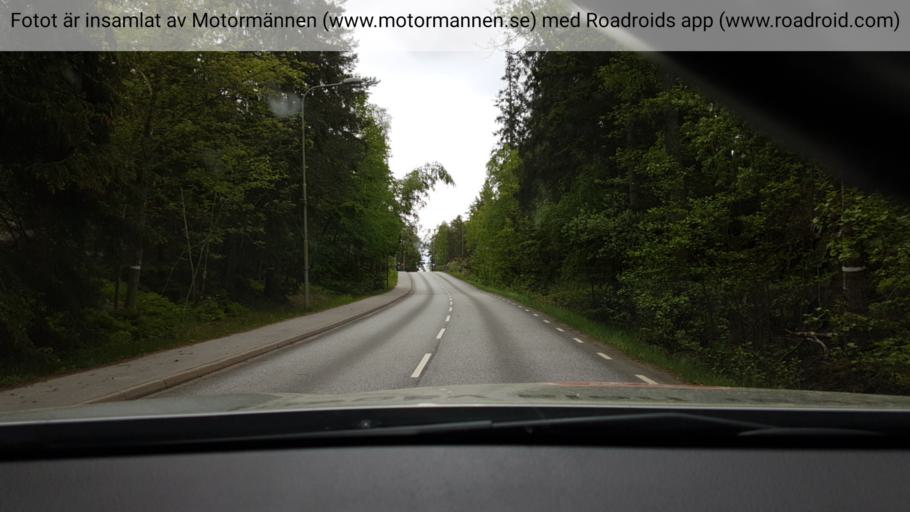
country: SE
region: Stockholm
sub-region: Nacka Kommun
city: Saltsjobaden
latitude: 59.2618
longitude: 18.3177
